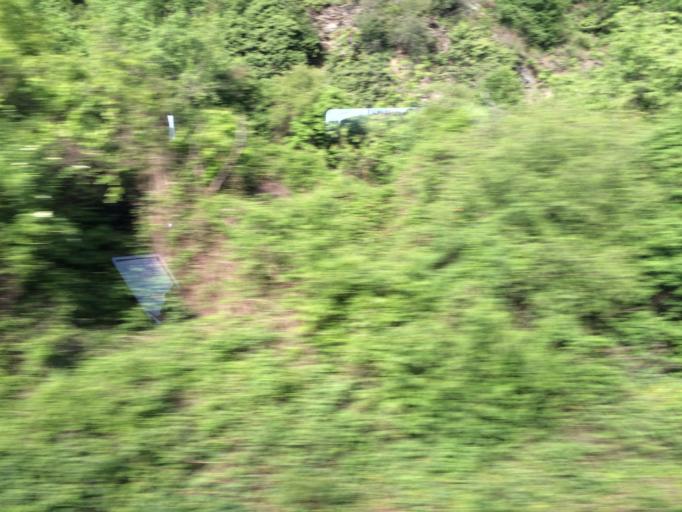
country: DE
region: Rheinland-Pfalz
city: Kestert
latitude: 50.2035
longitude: 7.6451
